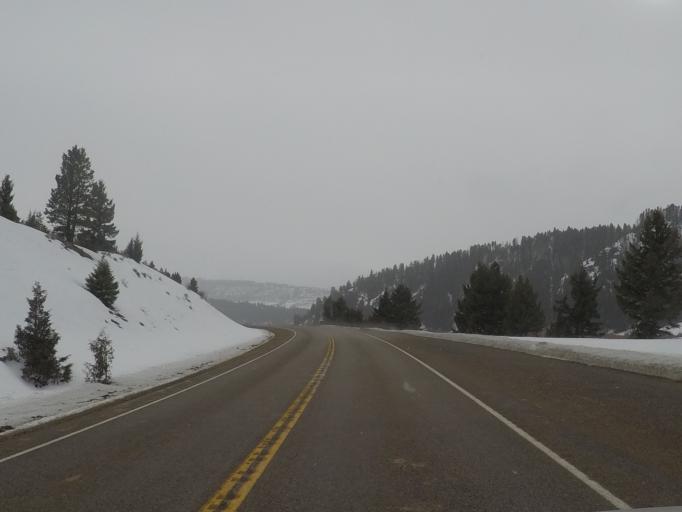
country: US
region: Montana
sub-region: Meagher County
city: White Sulphur Springs
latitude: 46.6784
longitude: -110.8776
